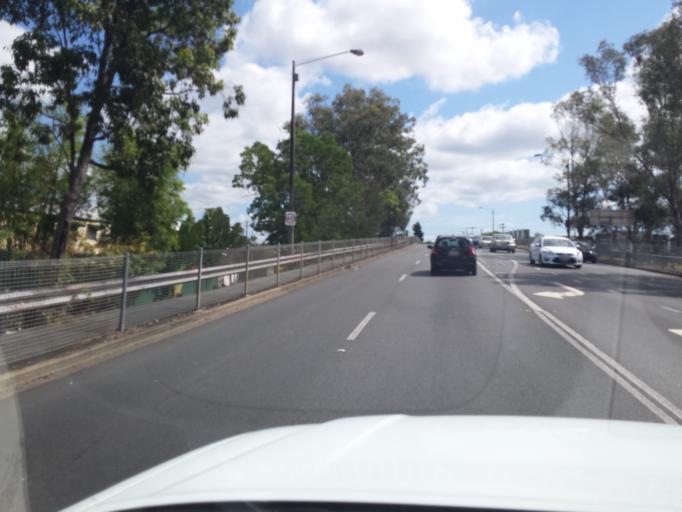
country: AU
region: Queensland
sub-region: Brisbane
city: Zillmere
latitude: -27.3616
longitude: 153.0378
